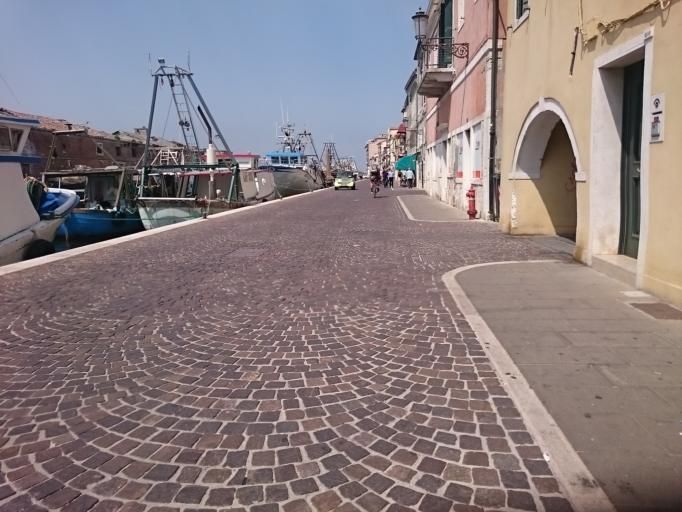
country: IT
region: Veneto
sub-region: Provincia di Venezia
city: Chioggia
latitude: 45.2205
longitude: 12.2768
